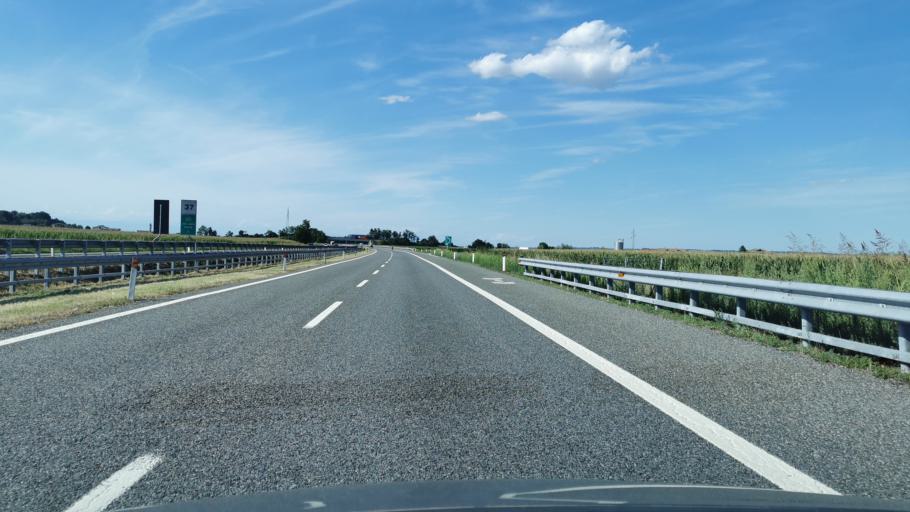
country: IT
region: Piedmont
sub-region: Provincia di Cuneo
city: Cervere
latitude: 44.6400
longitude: 7.7789
